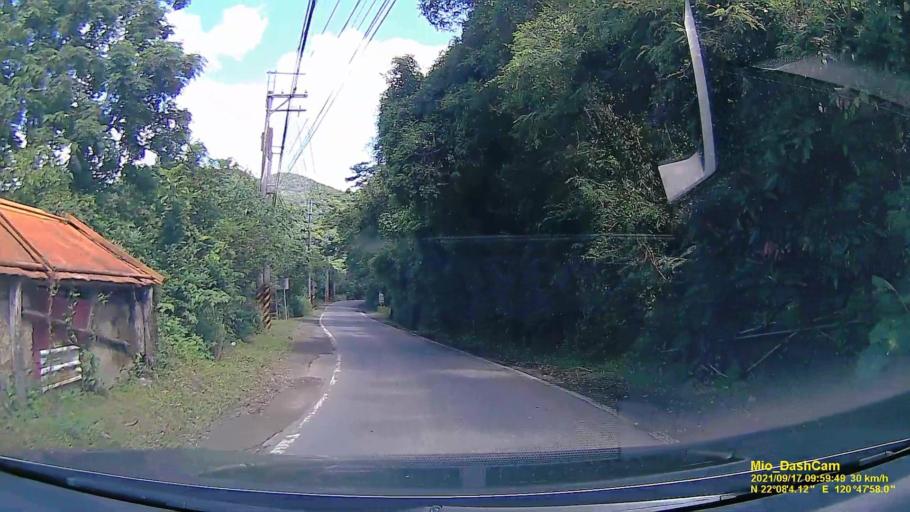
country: TW
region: Taiwan
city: Hengchun
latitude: 22.1345
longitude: 120.7994
